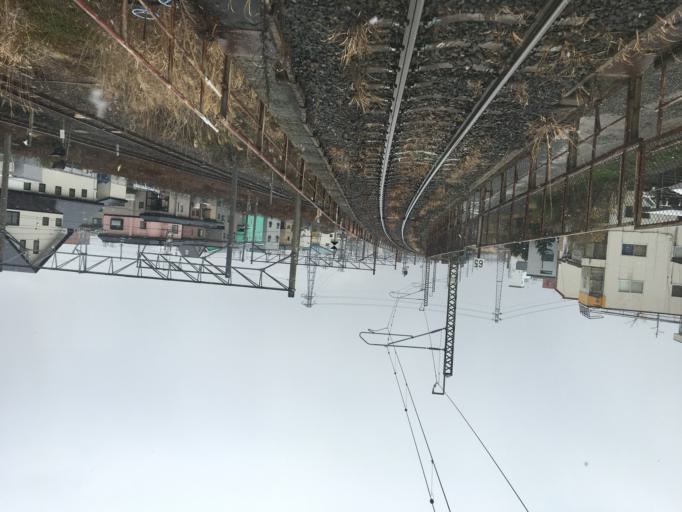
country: JP
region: Aomori
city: Aomori Shi
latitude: 40.8209
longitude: 140.7335
